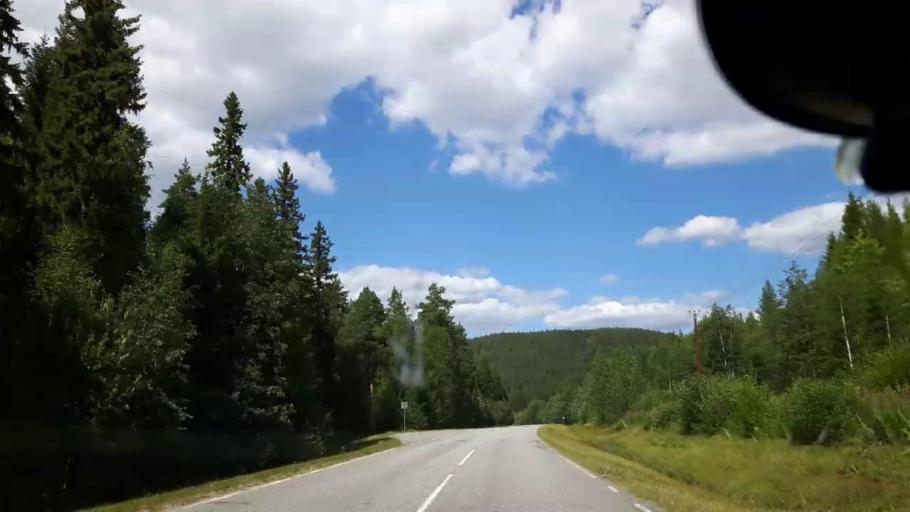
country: SE
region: Vaesternorrland
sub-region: Ange Kommun
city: Fransta
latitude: 62.7337
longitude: 16.3297
